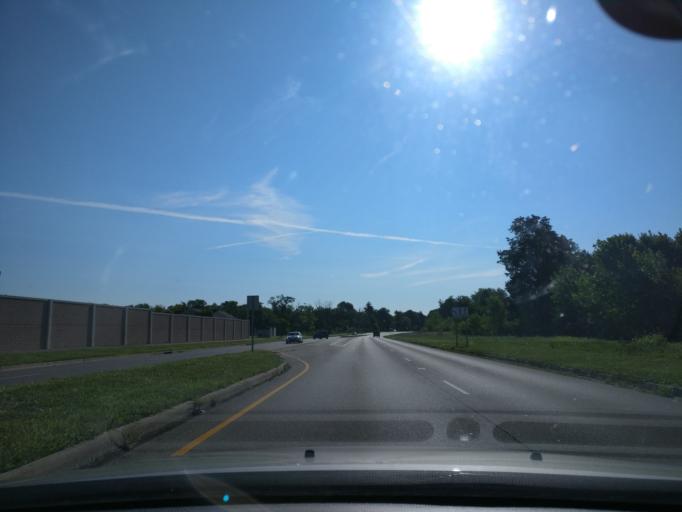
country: US
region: Ohio
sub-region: Warren County
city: Five Points
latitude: 39.5975
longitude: -84.2135
